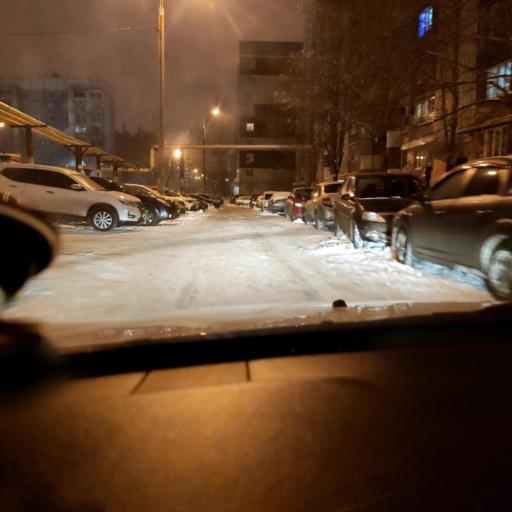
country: RU
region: Samara
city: Petra-Dubrava
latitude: 53.2993
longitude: 50.2746
